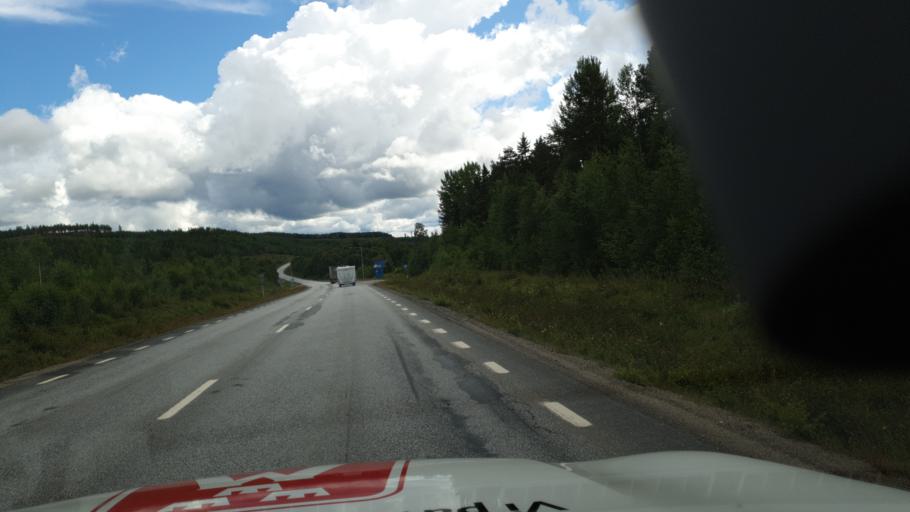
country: SE
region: Vaesterbotten
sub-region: Vannas Kommun
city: Vaennaes
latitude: 63.9999
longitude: 19.7237
